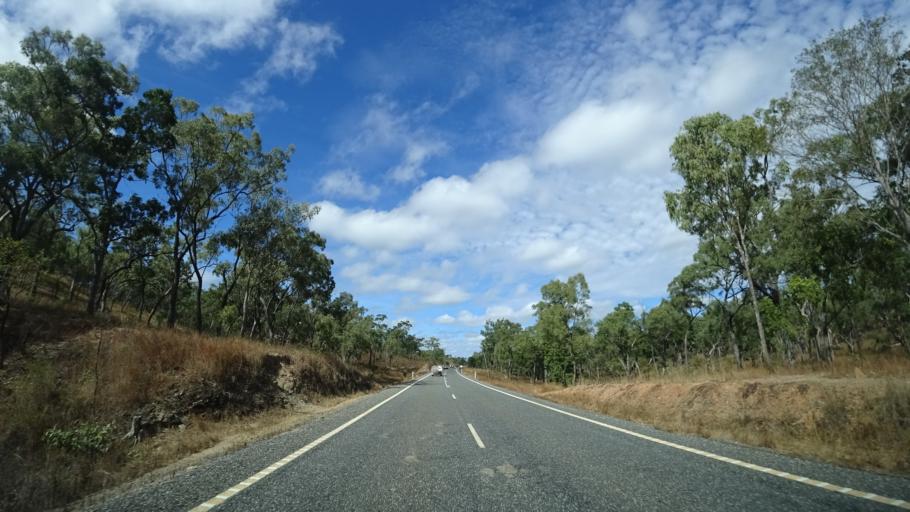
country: AU
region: Queensland
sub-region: Cairns
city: Port Douglas
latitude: -16.3067
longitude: 144.7169
